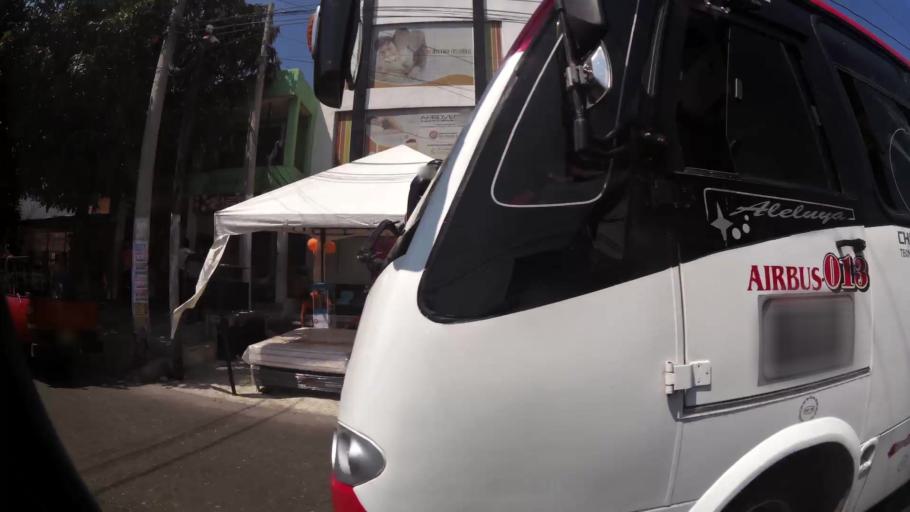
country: CO
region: Atlantico
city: Barranquilla
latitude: 10.9586
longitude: -74.8035
